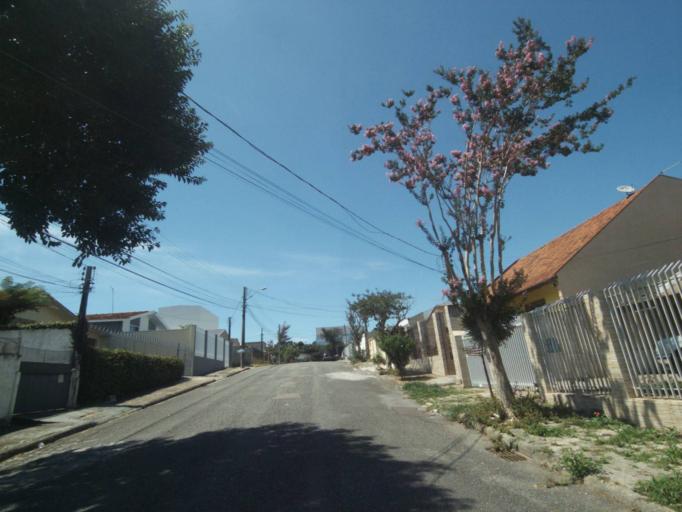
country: BR
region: Parana
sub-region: Curitiba
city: Curitiba
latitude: -25.4663
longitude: -49.2396
